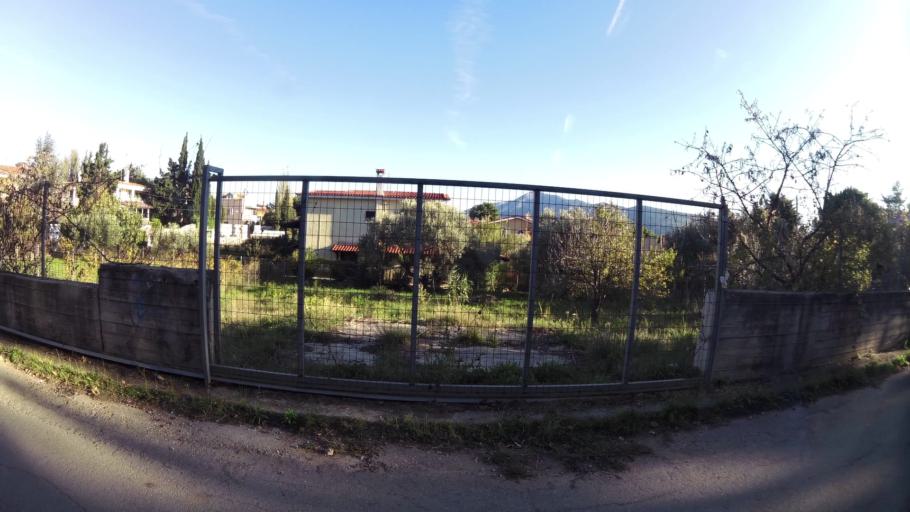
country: GR
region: Attica
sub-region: Nomarchia Anatolikis Attikis
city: Anoixi
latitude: 38.1376
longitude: 23.8509
